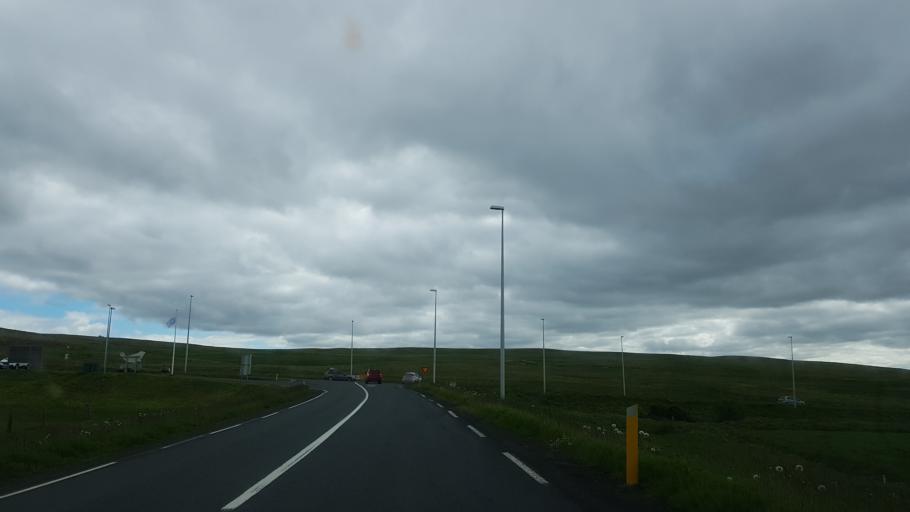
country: IS
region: Northwest
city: Saudarkrokur
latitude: 65.3530
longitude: -20.8860
